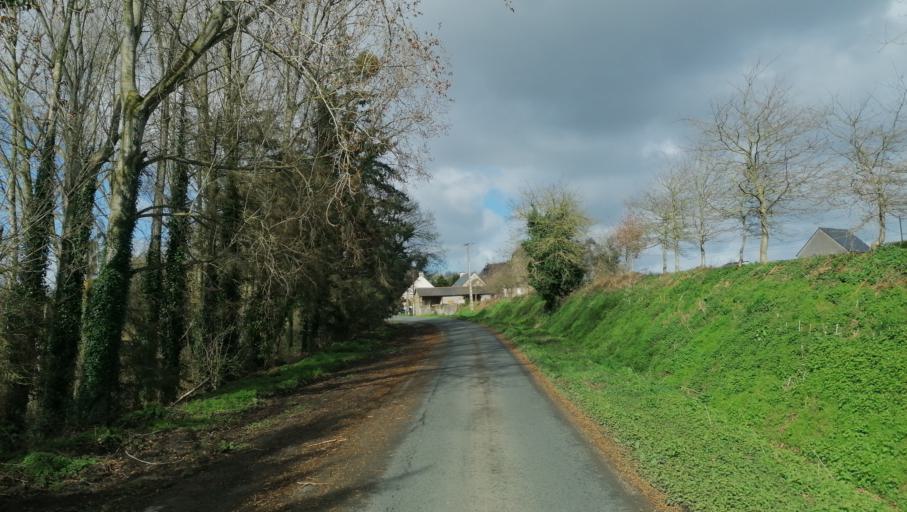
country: FR
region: Brittany
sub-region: Departement des Cotes-d'Armor
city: Plelo
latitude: 48.5764
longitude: -2.9162
